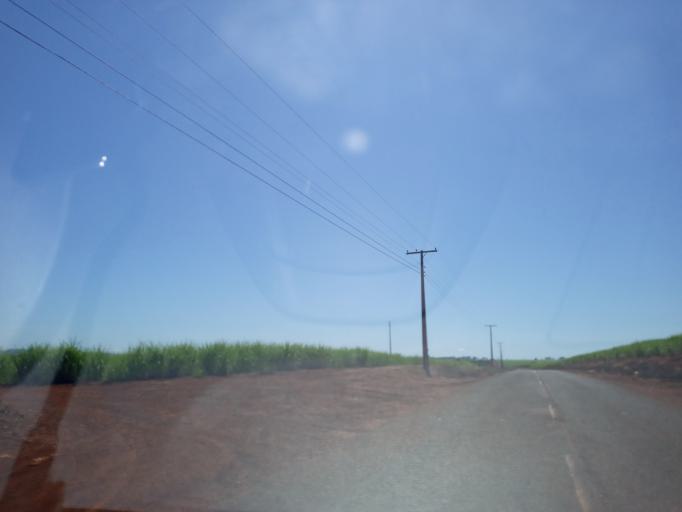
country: BR
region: Goias
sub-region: Itumbiara
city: Itumbiara
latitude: -18.4247
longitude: -49.1673
